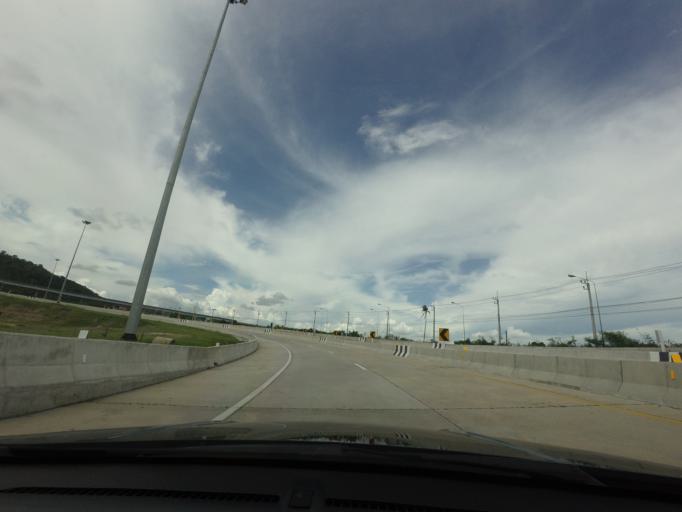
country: TH
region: Rayong
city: Ban Chang
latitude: 12.7094
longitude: 101.0289
